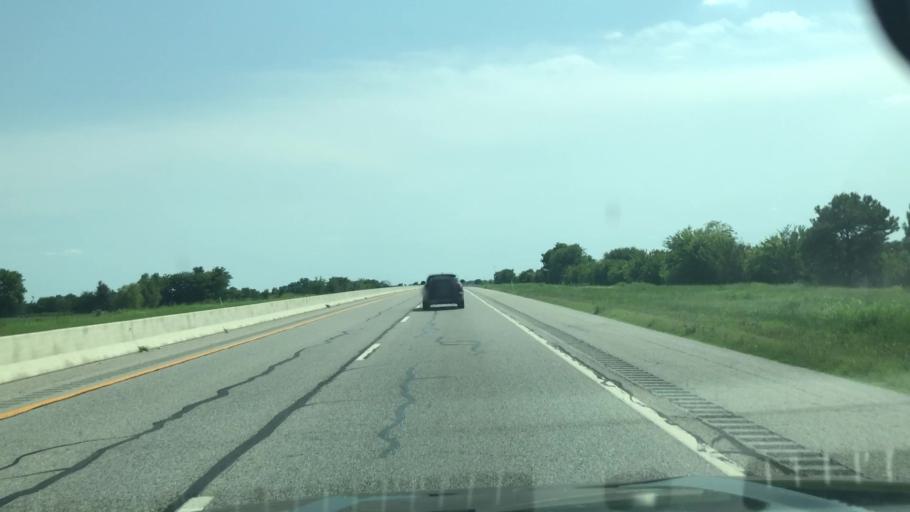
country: US
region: Oklahoma
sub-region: Ottawa County
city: Fairland
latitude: 36.8001
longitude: -94.8808
